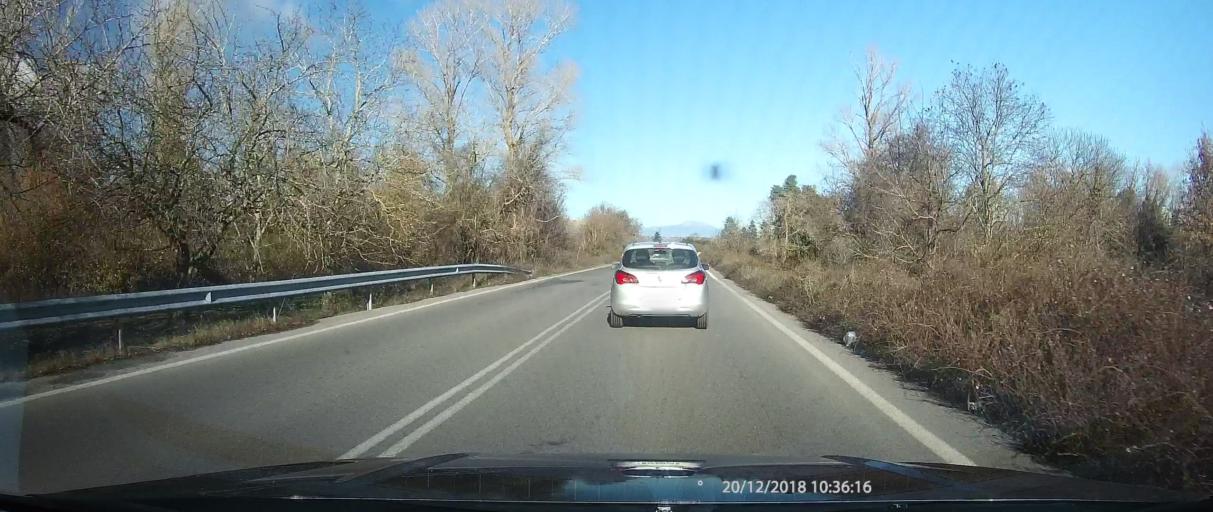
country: GR
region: Peloponnese
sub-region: Nomos Lakonias
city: Kariai
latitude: 37.3637
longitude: 22.4027
